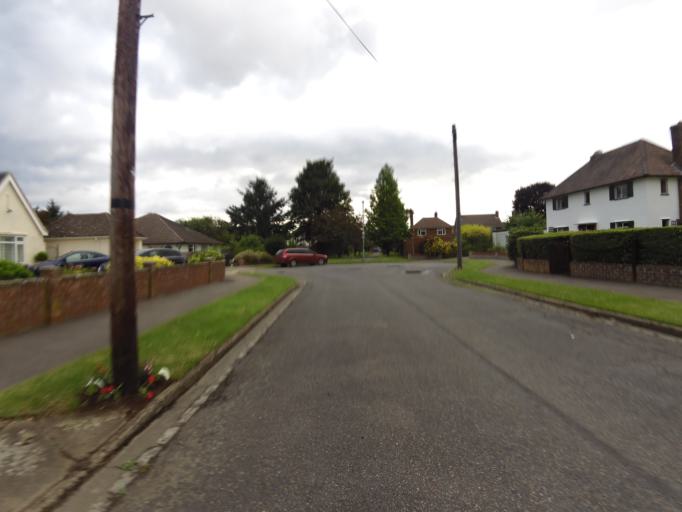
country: GB
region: England
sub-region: Suffolk
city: Ipswich
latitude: 52.0704
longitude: 1.1587
